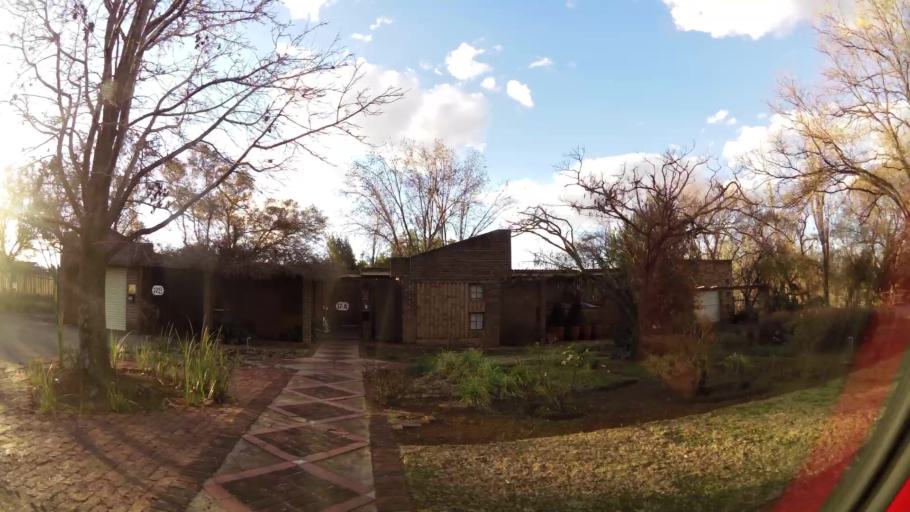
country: ZA
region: North-West
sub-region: Dr Kenneth Kaunda District Municipality
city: Potchefstroom
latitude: -26.6831
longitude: 27.0979
